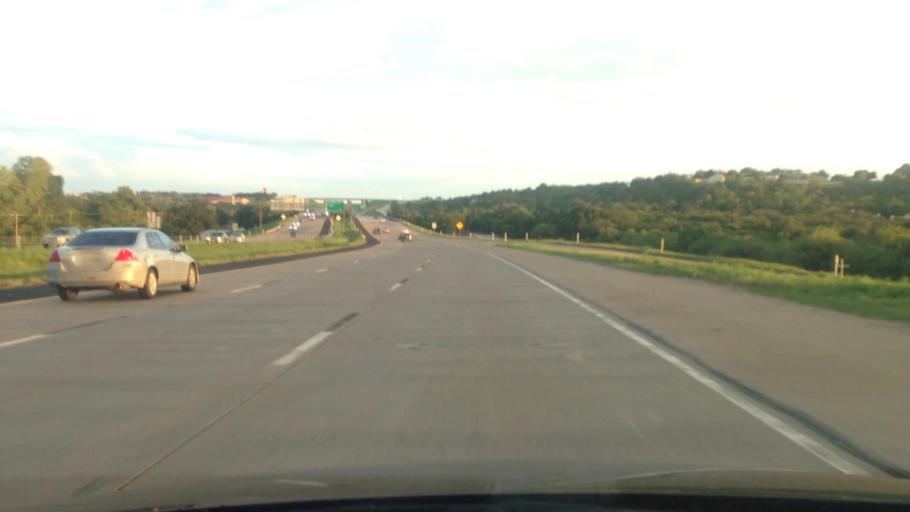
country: US
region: Texas
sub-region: Tarrant County
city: Benbrook
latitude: 32.7161
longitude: -97.4790
